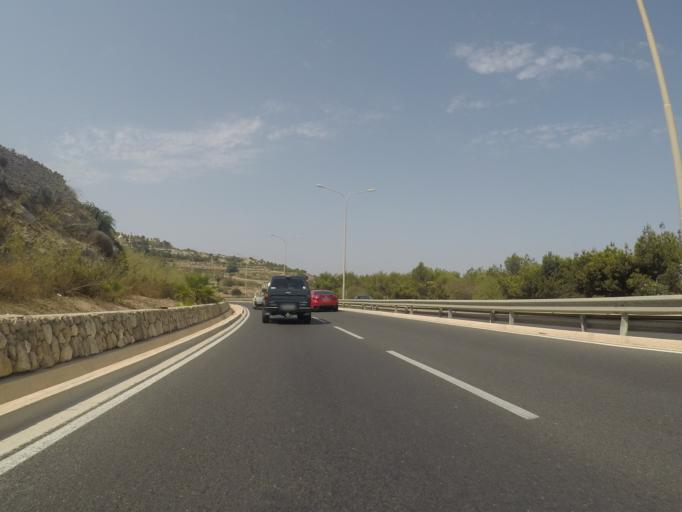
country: MT
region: Saint Paul's Bay
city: San Pawl il-Bahar
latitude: 35.9455
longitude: 14.3929
